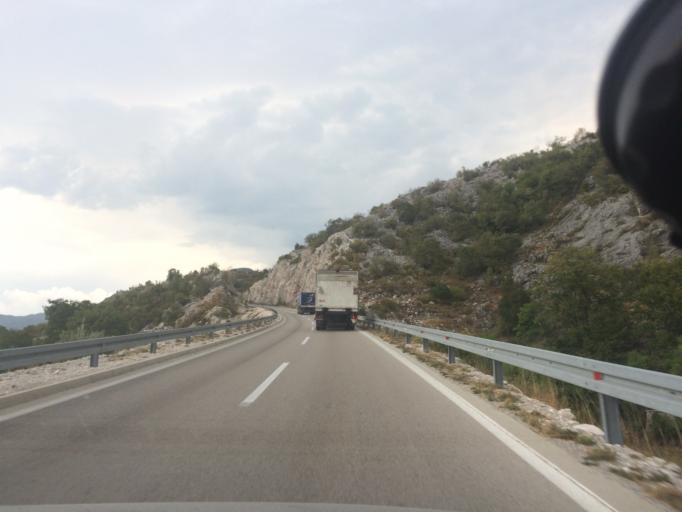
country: ME
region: Kotor
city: Risan
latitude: 42.6547
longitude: 18.6751
